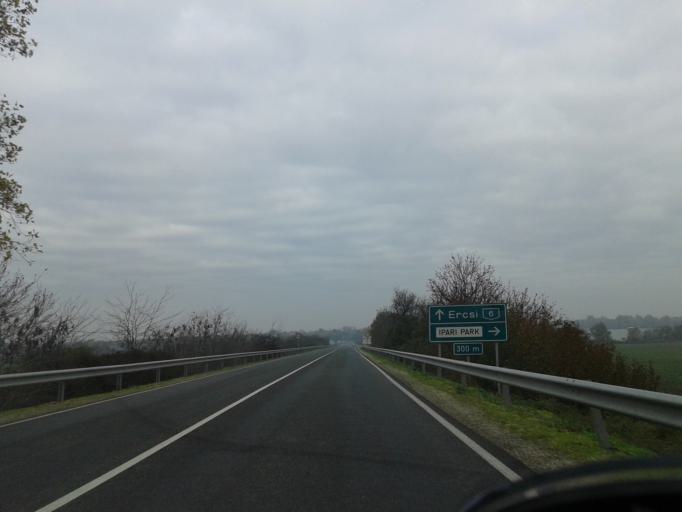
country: HU
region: Fejer
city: Ercsi
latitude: 47.2329
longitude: 18.8920
